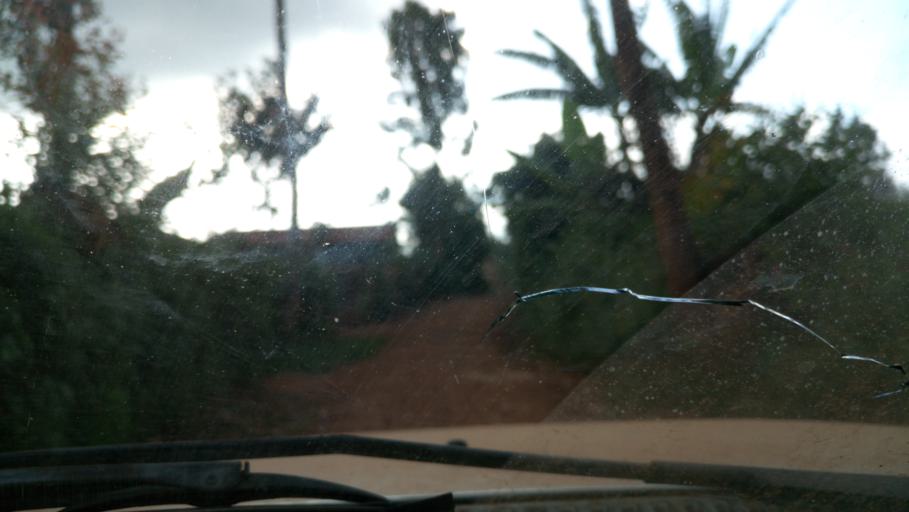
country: KE
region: Murang'a District
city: Kangema
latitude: -0.8532
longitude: 36.9394
